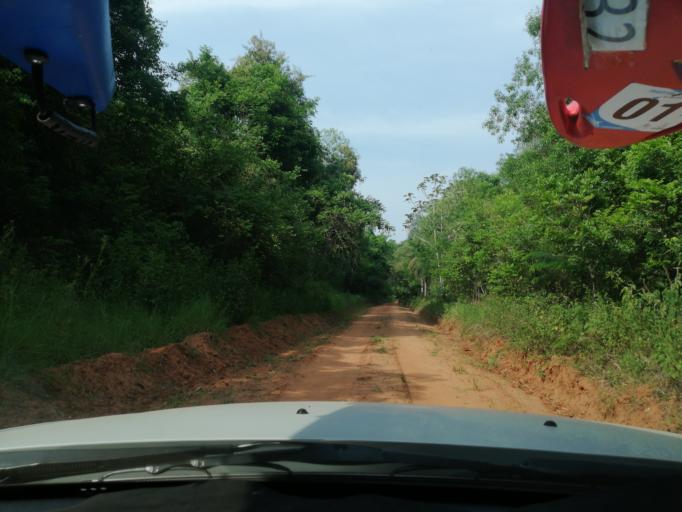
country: AR
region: Misiones
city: Santa Ana
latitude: -27.3051
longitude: -55.5808
